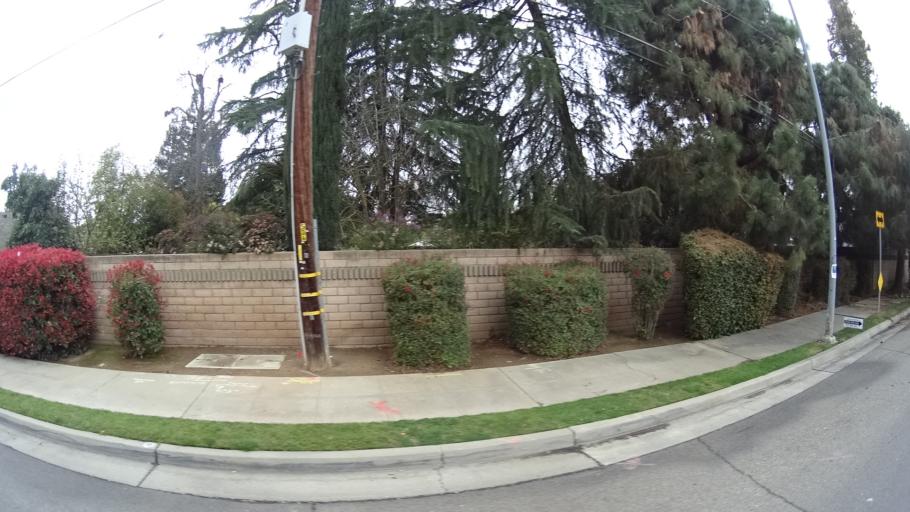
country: US
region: California
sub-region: Fresno County
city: Fresno
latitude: 36.8443
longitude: -119.8477
